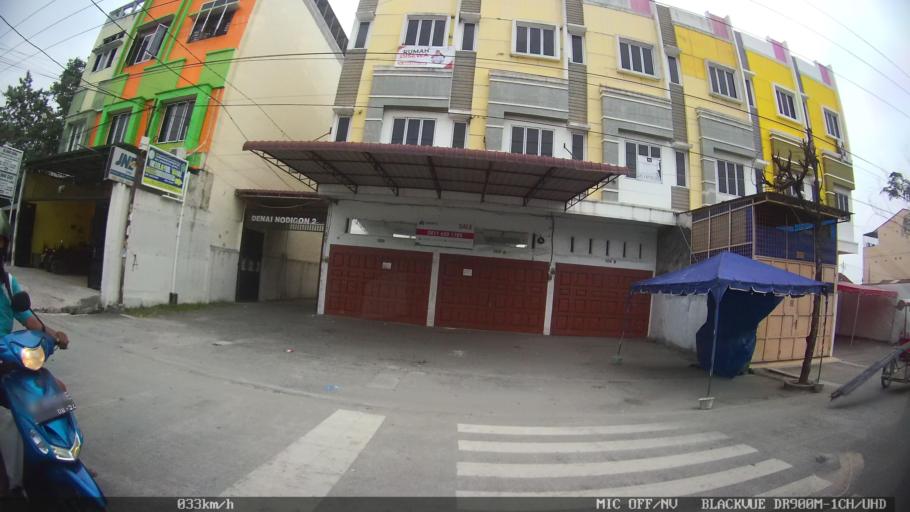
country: ID
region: North Sumatra
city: Medan
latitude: 3.5818
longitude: 98.7154
